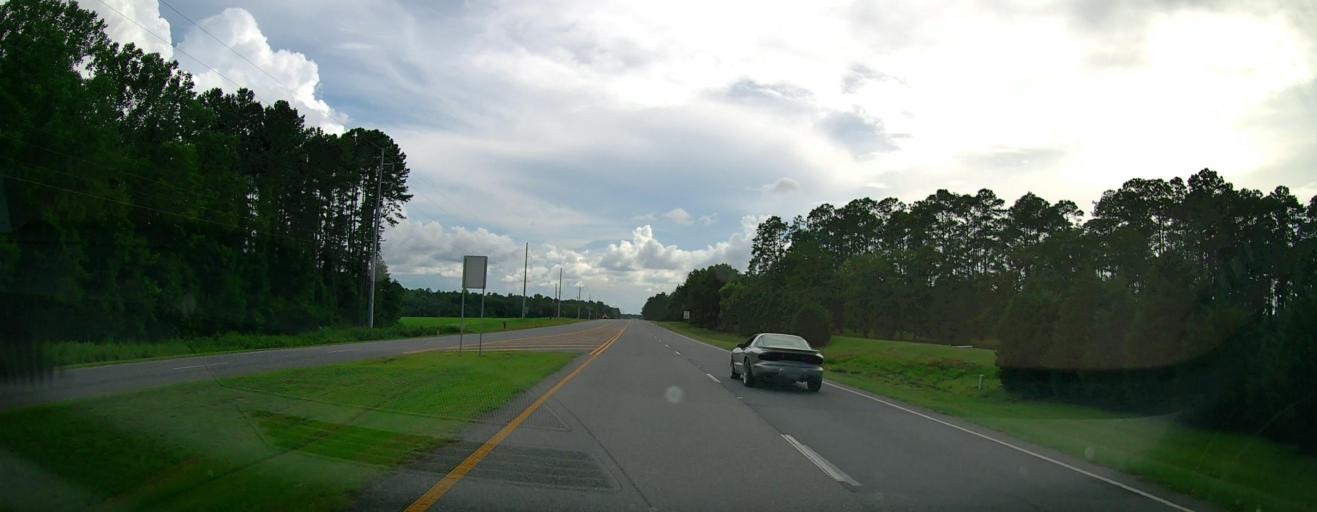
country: US
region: Georgia
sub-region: Wayne County
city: Jesup
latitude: 31.4799
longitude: -82.0254
